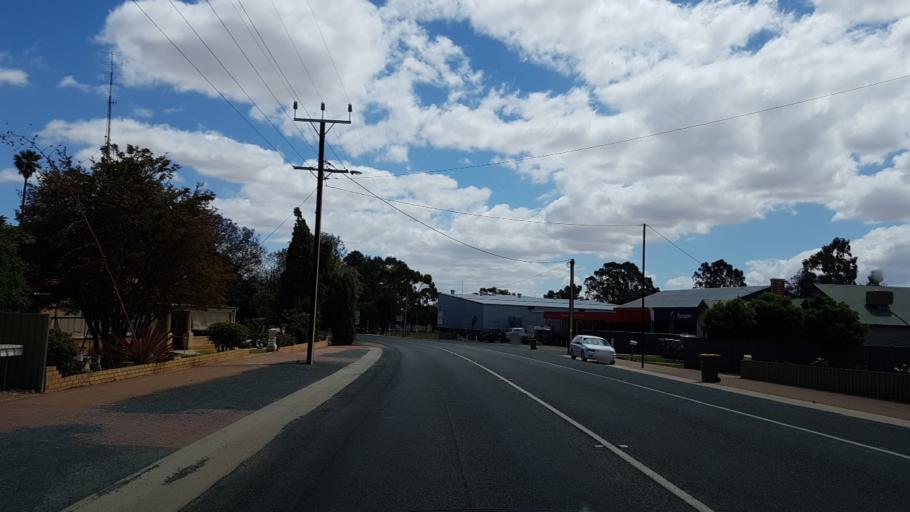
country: AU
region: South Australia
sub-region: Loxton Waikerie
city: Waikerie
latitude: -34.1817
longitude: 139.9832
